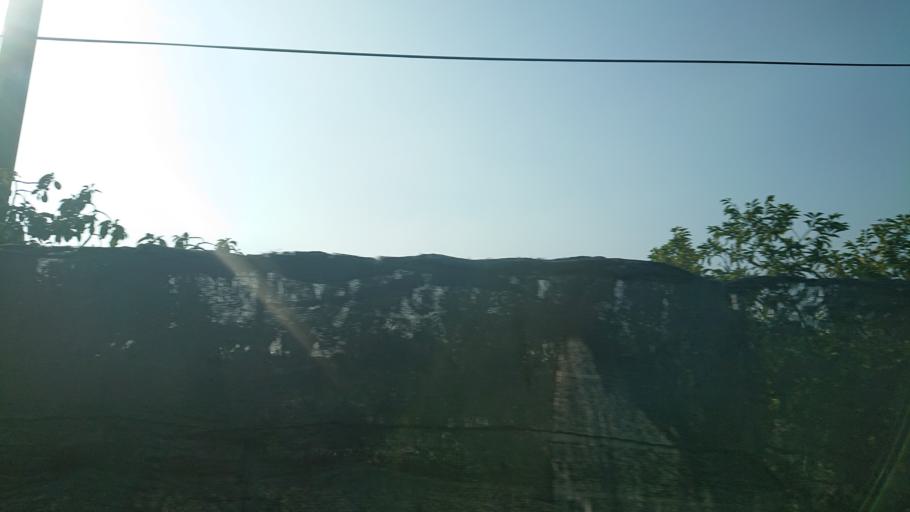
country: TW
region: Taiwan
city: Xinying
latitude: 23.1539
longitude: 120.2491
